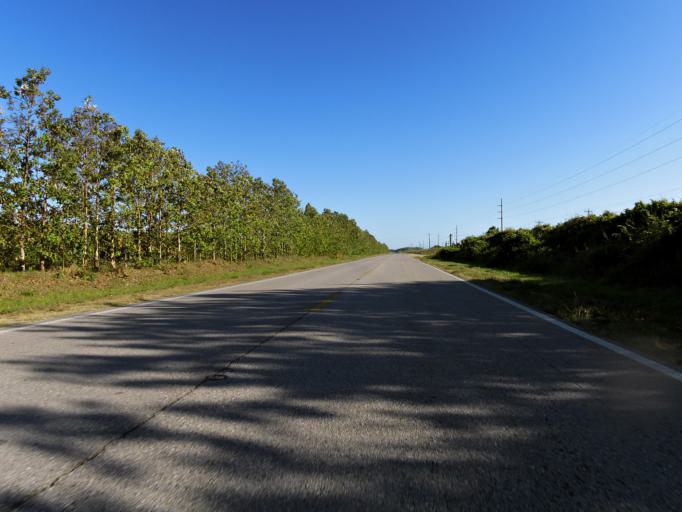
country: US
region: Florida
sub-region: Collier County
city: Immokalee
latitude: 26.3259
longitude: -81.4165
